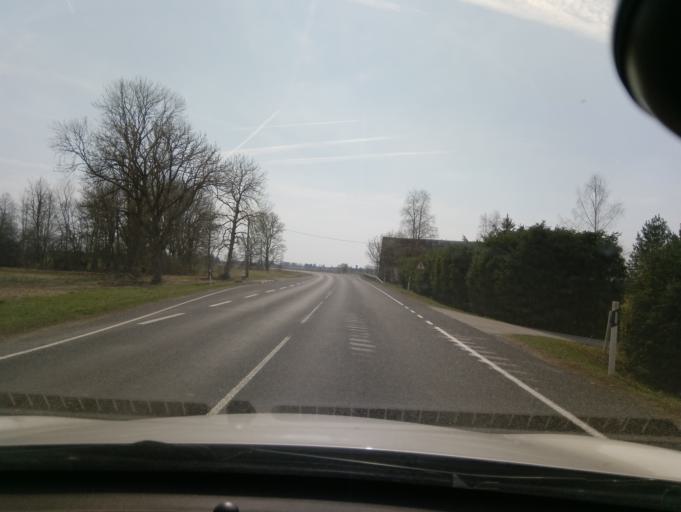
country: EE
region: Viljandimaa
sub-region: Vohma linn
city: Vohma
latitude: 58.6762
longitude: 25.6053
